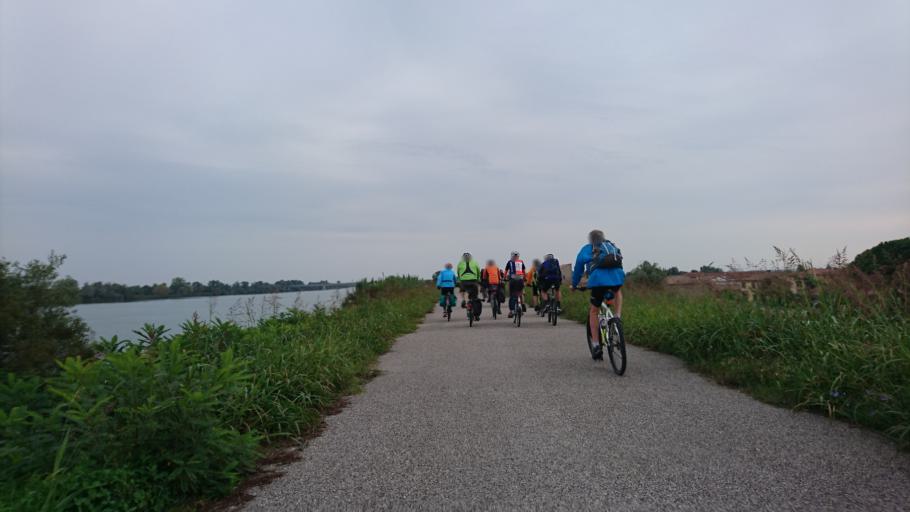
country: IT
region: Veneto
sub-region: Provincia di Rovigo
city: Ca' Tiepolo
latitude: 44.9539
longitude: 12.3473
